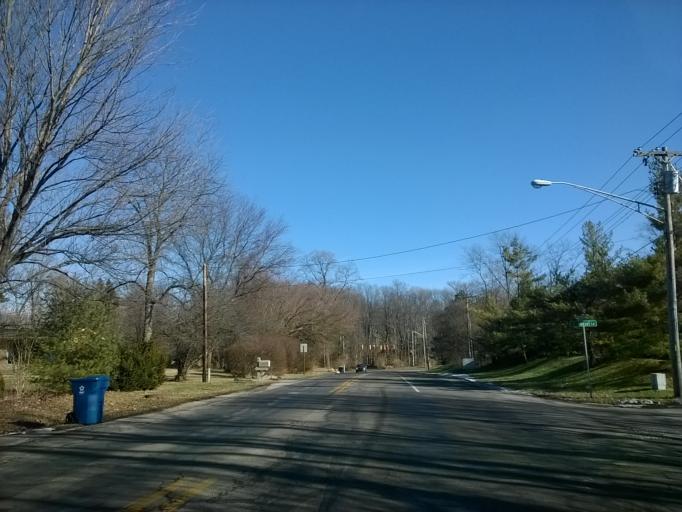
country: US
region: Indiana
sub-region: Marion County
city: Meridian Hills
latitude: 39.8976
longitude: -86.1669
